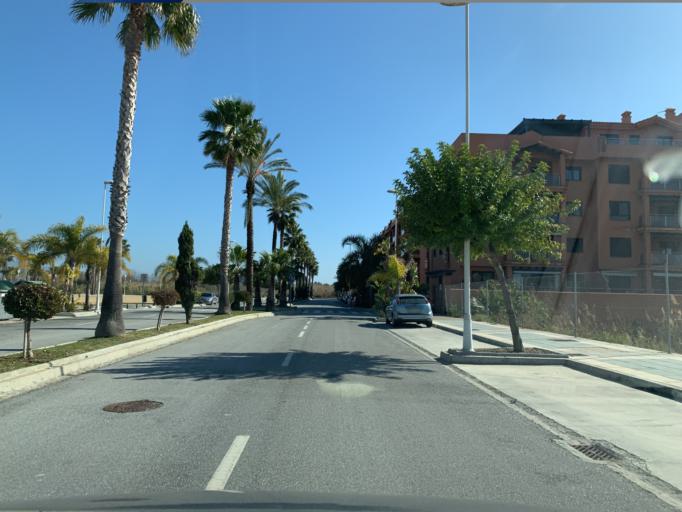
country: ES
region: Andalusia
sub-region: Provincia de Granada
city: El Varadero
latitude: 36.7202
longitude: -3.5515
